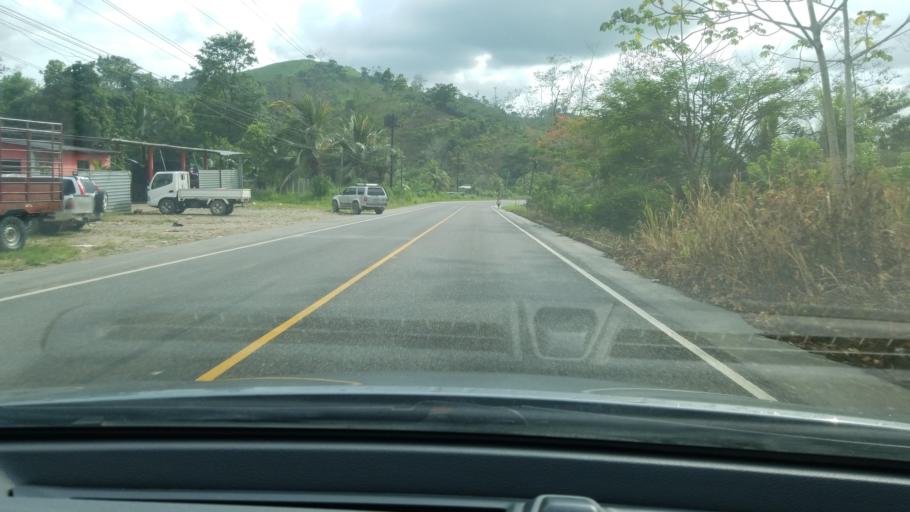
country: HN
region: Cortes
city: Potrerillos
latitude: 15.5941
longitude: -88.3077
